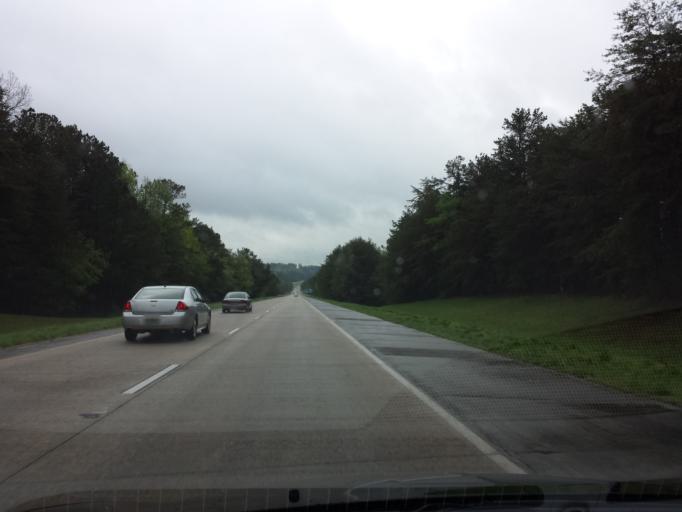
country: US
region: Georgia
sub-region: Cherokee County
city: Ball Ground
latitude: 34.3531
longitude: -84.3917
